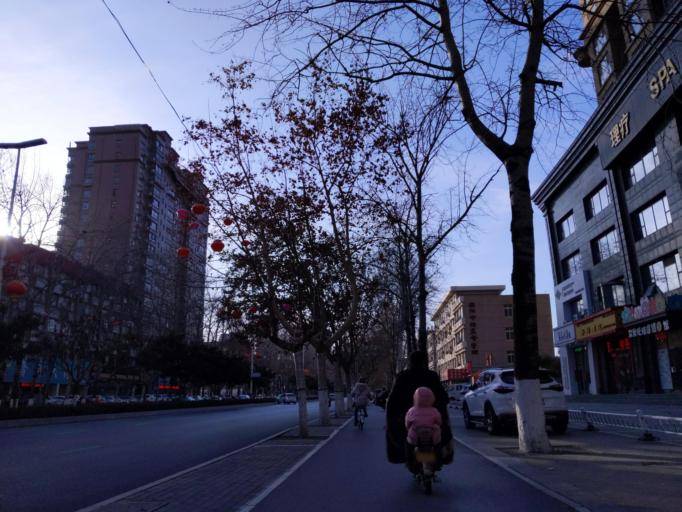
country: CN
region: Henan Sheng
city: Puyang
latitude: 35.7618
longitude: 115.0174
